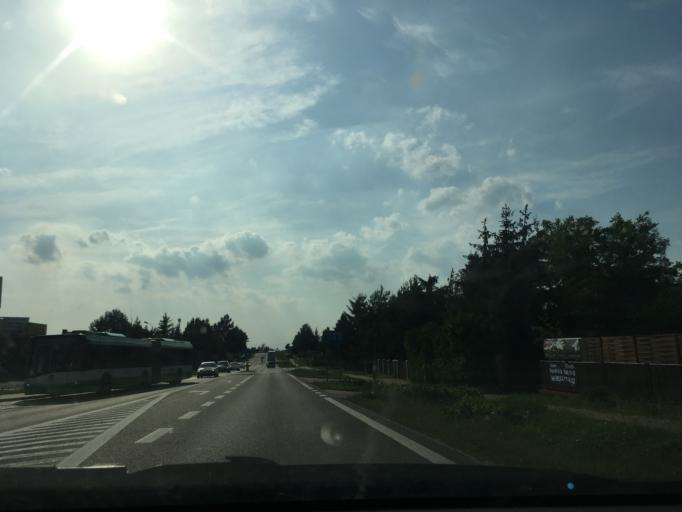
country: PL
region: Podlasie
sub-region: Powiat bialostocki
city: Wasilkow
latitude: 53.1253
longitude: 23.2547
